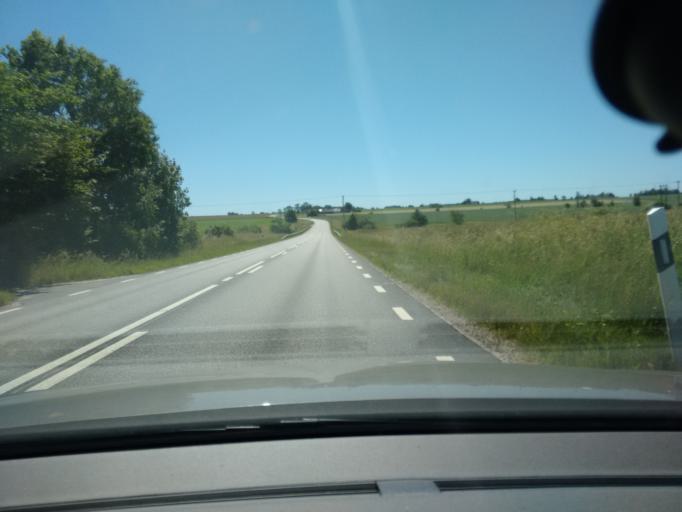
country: SE
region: Skane
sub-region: Horby Kommun
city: Hoerby
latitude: 55.8289
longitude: 13.6605
